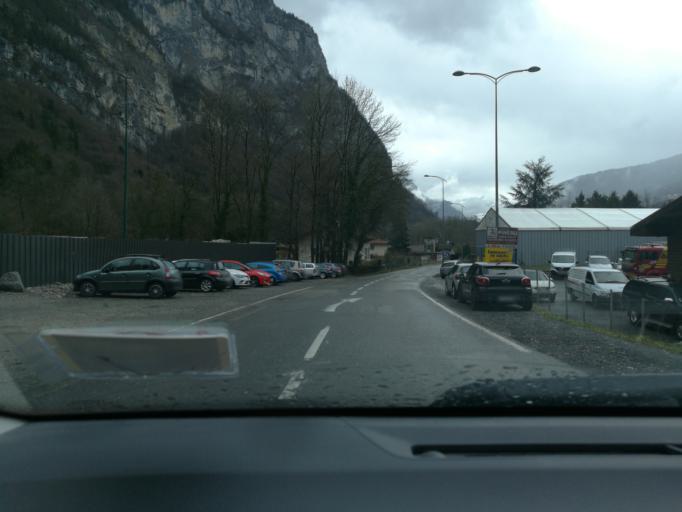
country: FR
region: Rhone-Alpes
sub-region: Departement de la Haute-Savoie
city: Araches-la-Frasse
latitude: 46.0407
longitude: 6.6130
